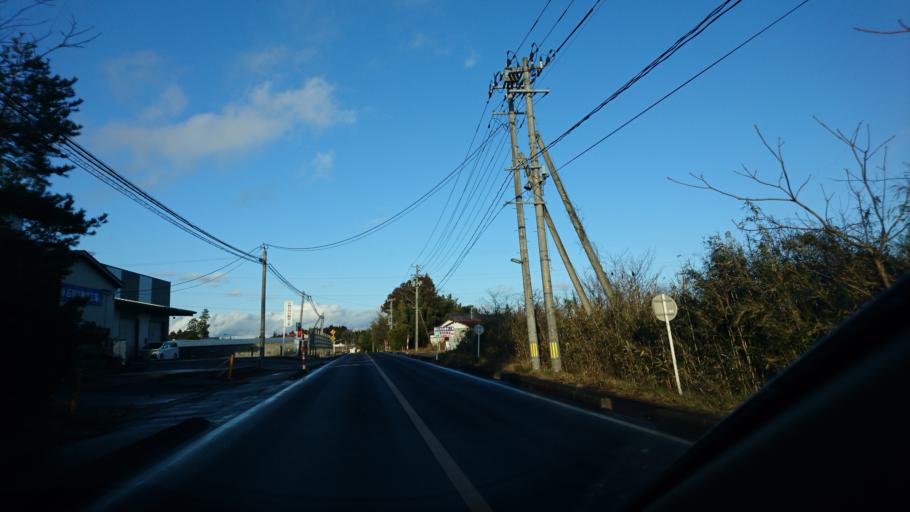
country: JP
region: Miyagi
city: Furukawa
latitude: 38.5986
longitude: 140.8654
